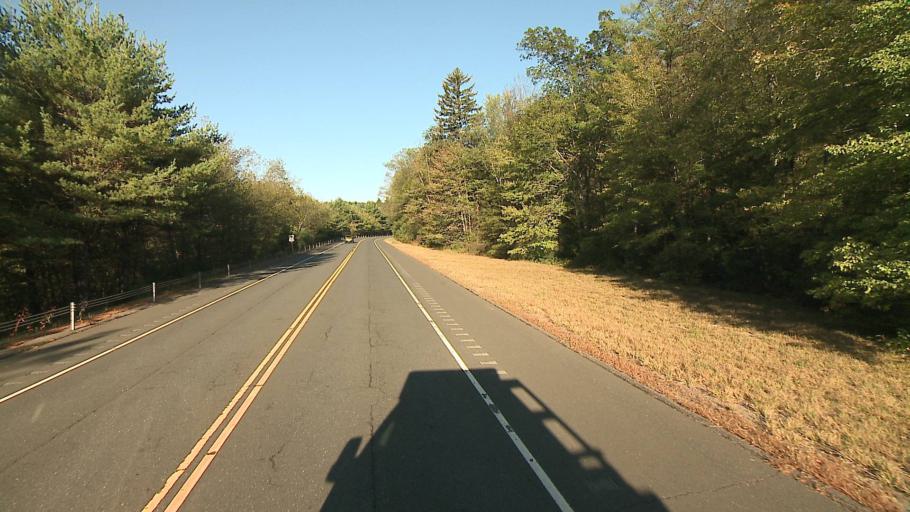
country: US
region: Connecticut
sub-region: Hartford County
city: Collinsville
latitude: 41.8196
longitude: -72.9659
